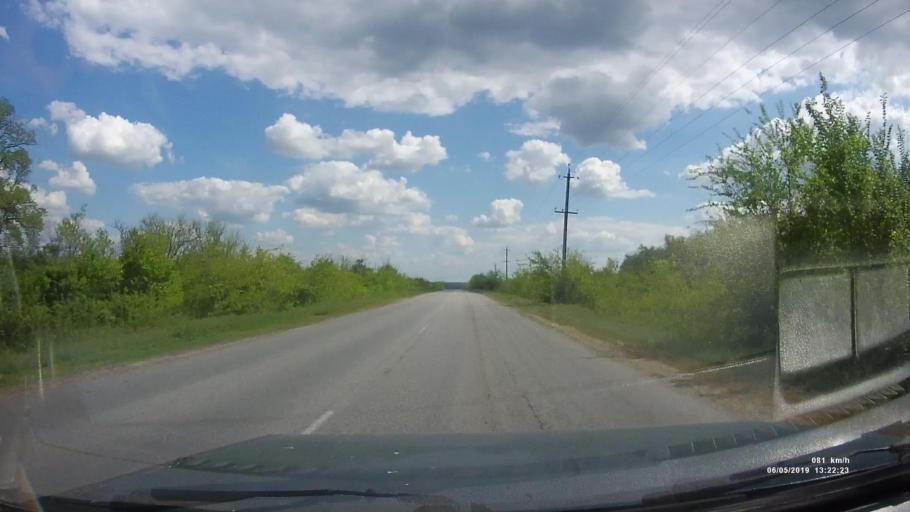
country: RU
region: Rostov
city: Ust'-Donetskiy
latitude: 47.6962
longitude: 40.9195
